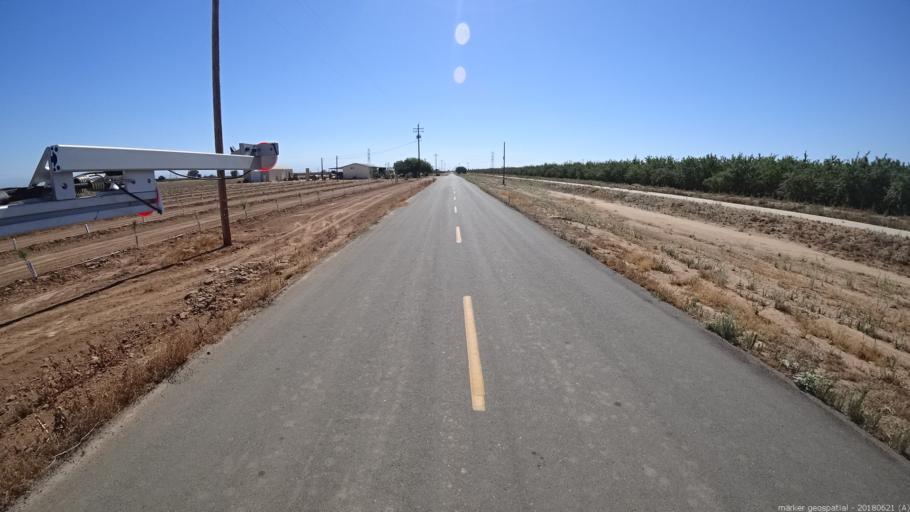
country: US
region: California
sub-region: Fresno County
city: Biola
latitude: 36.8658
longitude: -119.9419
